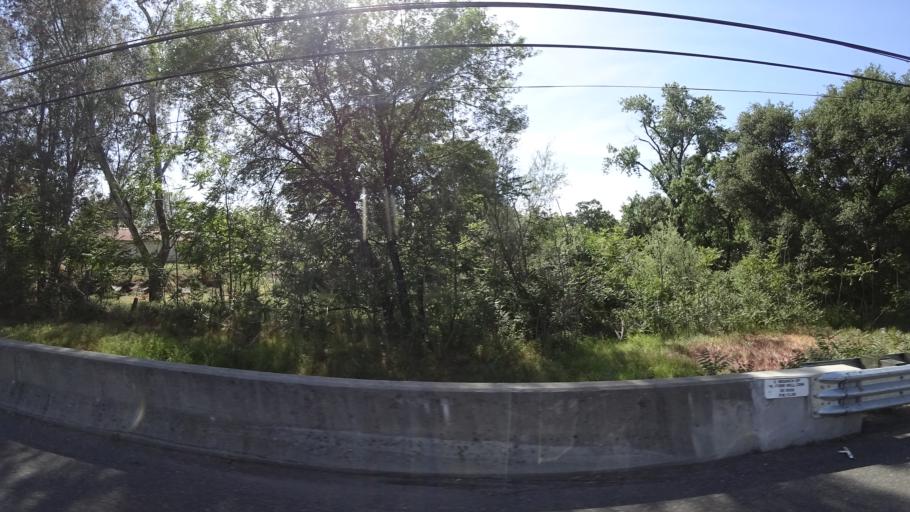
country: US
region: California
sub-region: Tehama County
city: Los Molinos
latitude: 40.0520
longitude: -122.1008
